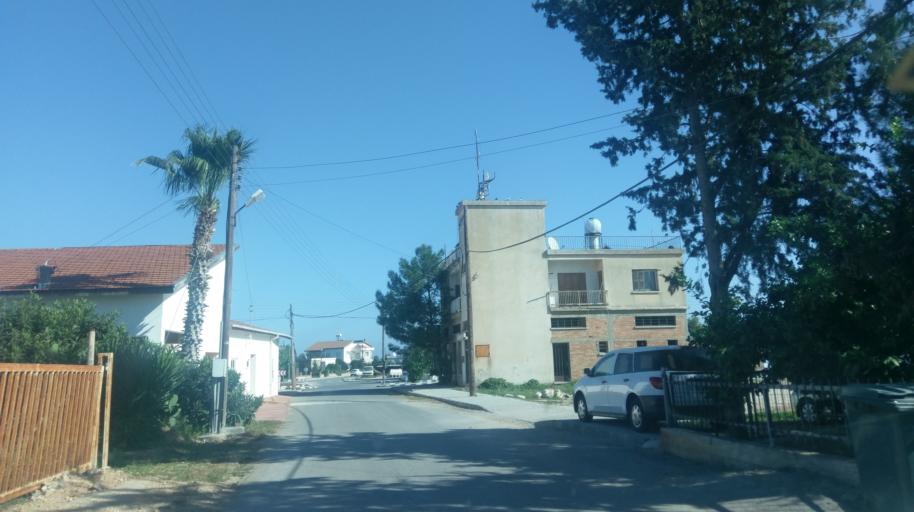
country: CY
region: Ammochostos
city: Trikomo
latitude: 35.2367
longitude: 33.8601
